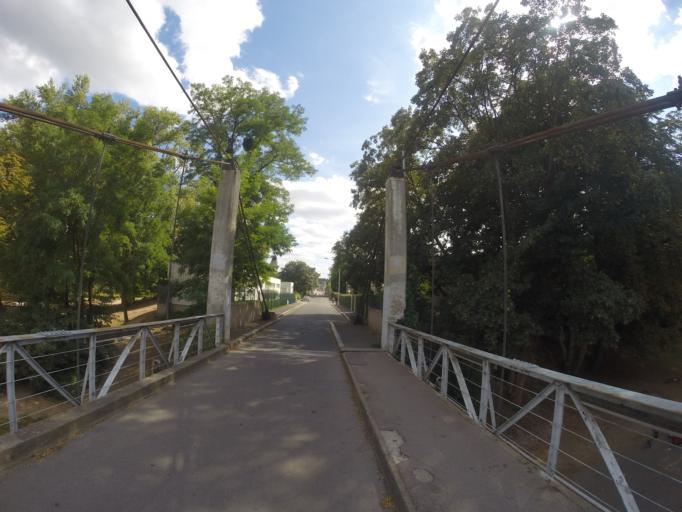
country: FR
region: Centre
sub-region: Departement d'Indre-et-Loire
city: Tours
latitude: 47.4011
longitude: 0.6932
